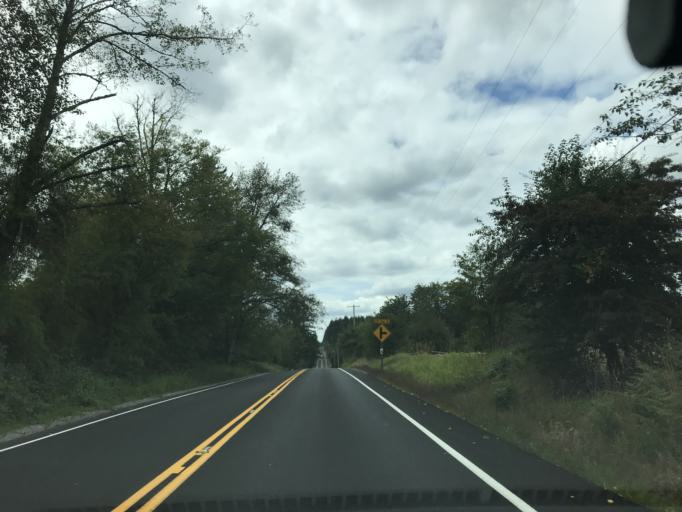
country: US
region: Washington
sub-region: King County
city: Black Diamond
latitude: 47.2867
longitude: -121.9977
